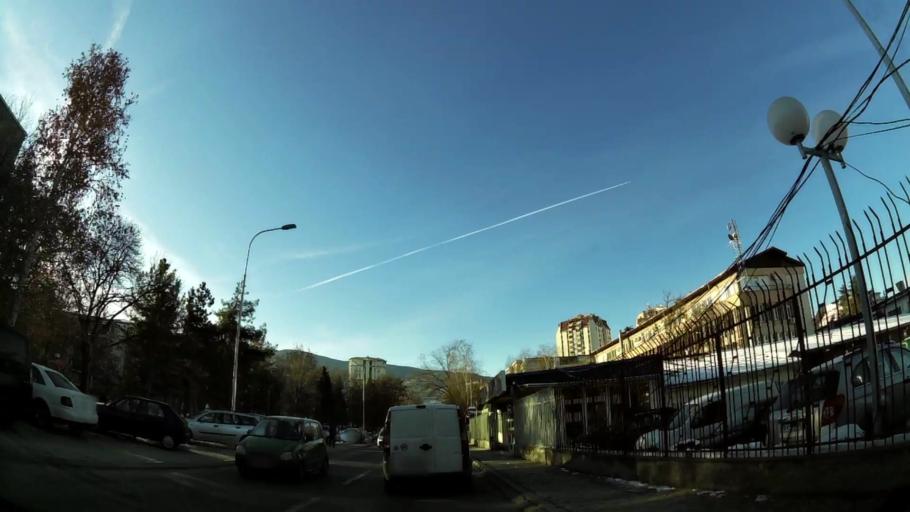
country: MK
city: Krushopek
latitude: 42.0076
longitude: 21.3838
